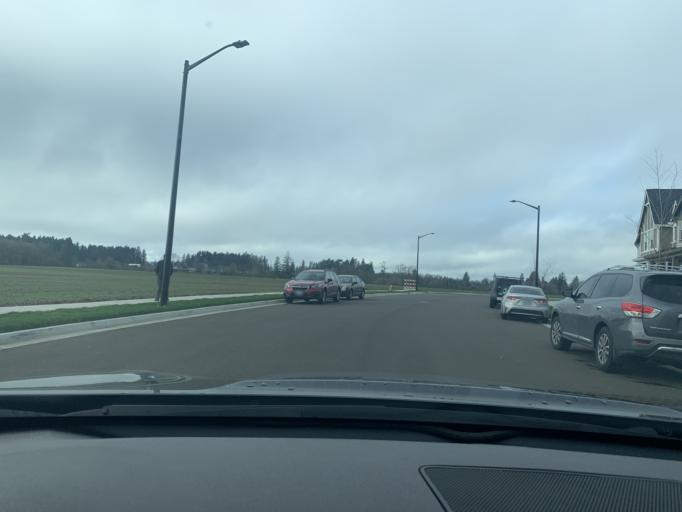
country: US
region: Oregon
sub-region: Washington County
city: North Plains
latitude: 45.5888
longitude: -122.9773
